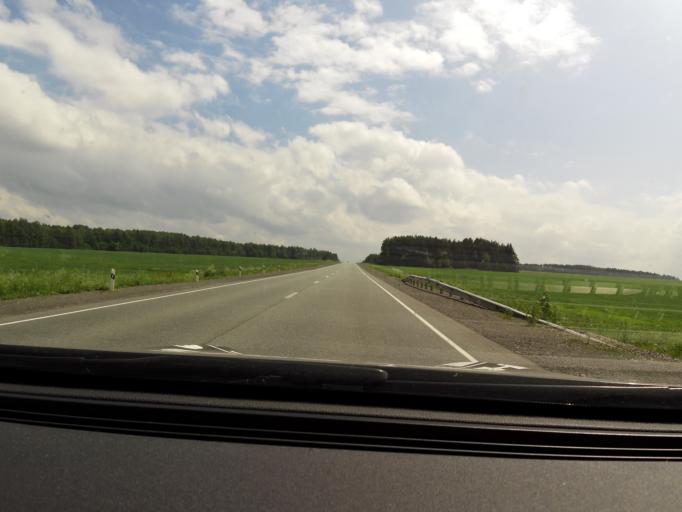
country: RU
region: Perm
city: Suksun
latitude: 57.0274
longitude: 57.4547
